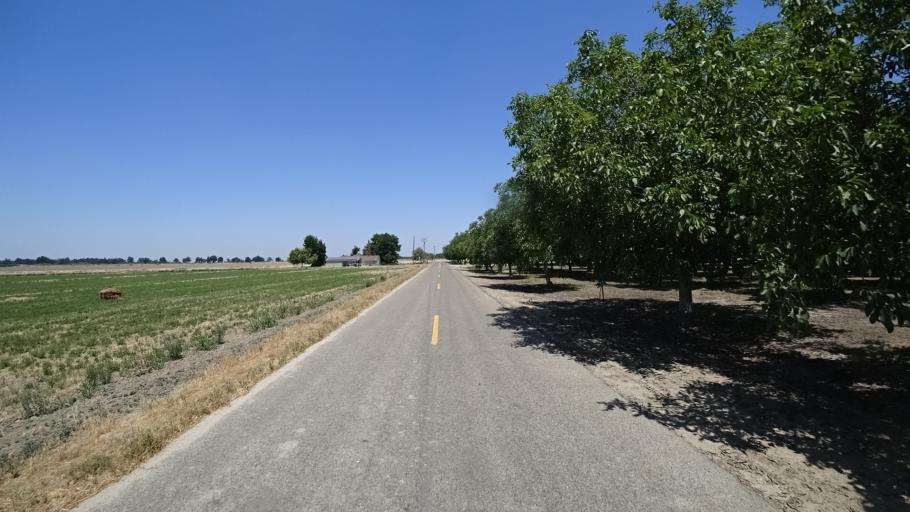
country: US
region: California
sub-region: Fresno County
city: Laton
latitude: 36.4087
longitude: -119.7269
